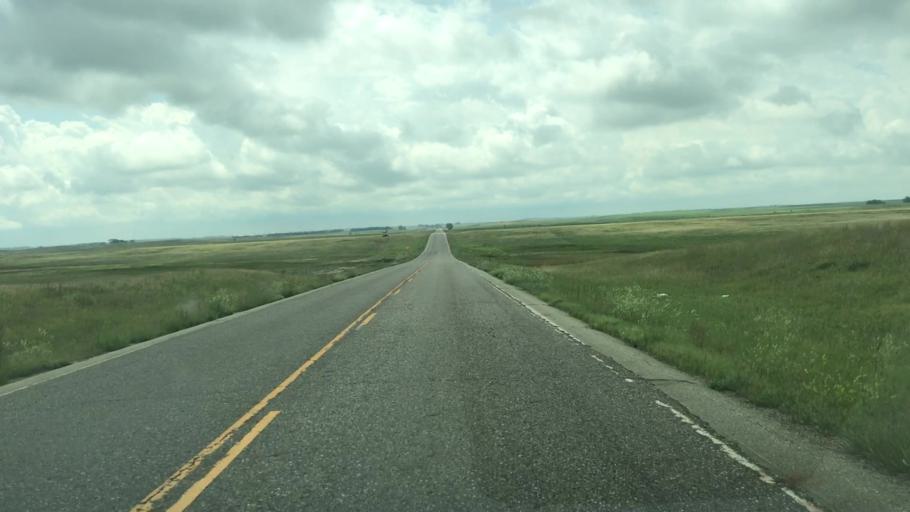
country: US
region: Nebraska
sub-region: Cherry County
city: Valentine
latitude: 43.0683
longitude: -100.5958
